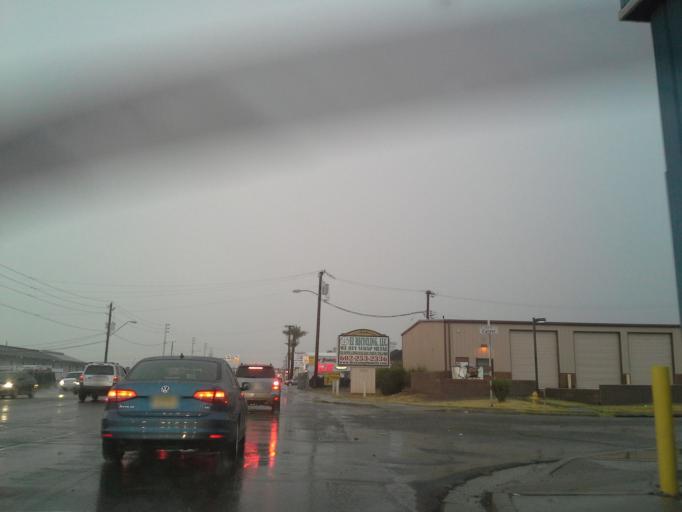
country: US
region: Arizona
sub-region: Maricopa County
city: Phoenix
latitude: 33.4629
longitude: -112.0999
